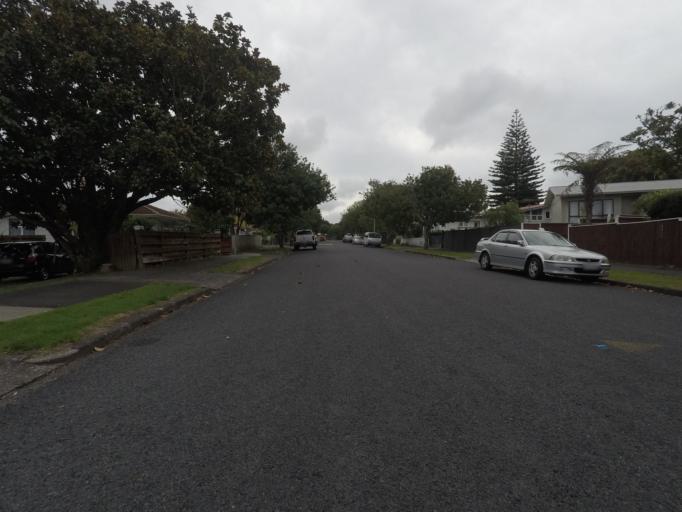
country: NZ
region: Auckland
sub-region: Auckland
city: Rosebank
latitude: -36.8917
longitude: 174.6778
